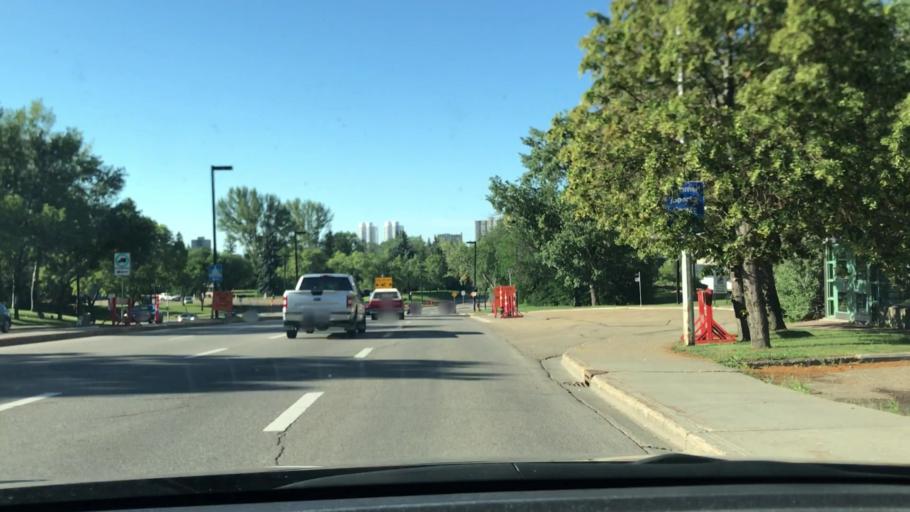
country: CA
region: Alberta
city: Edmonton
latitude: 53.5357
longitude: -113.5086
